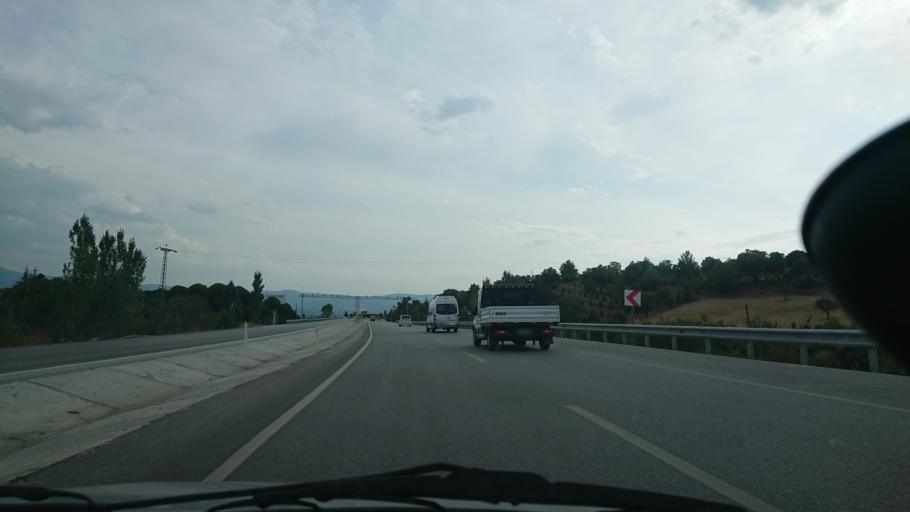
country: TR
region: Kuetahya
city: Gediz
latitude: 39.0143
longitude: 29.4097
